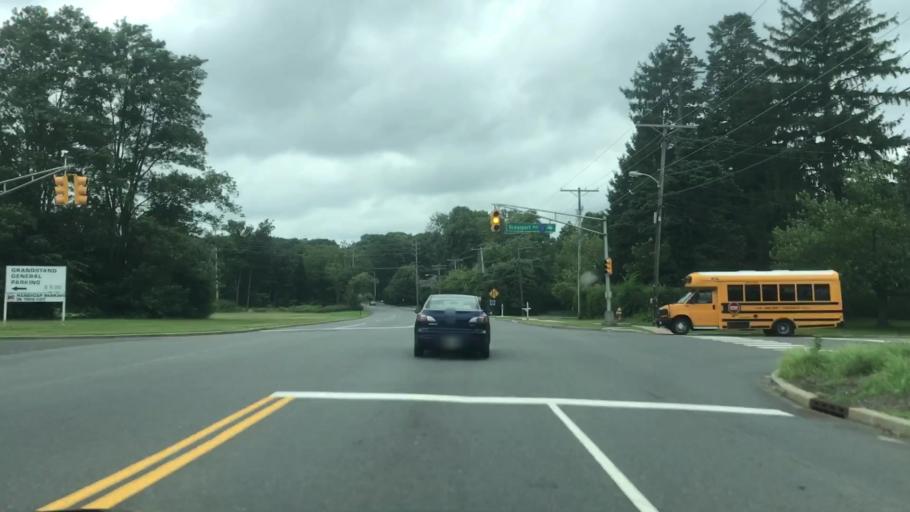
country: US
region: New Jersey
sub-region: Monmouth County
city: Oceanport
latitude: 40.3089
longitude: -74.0263
